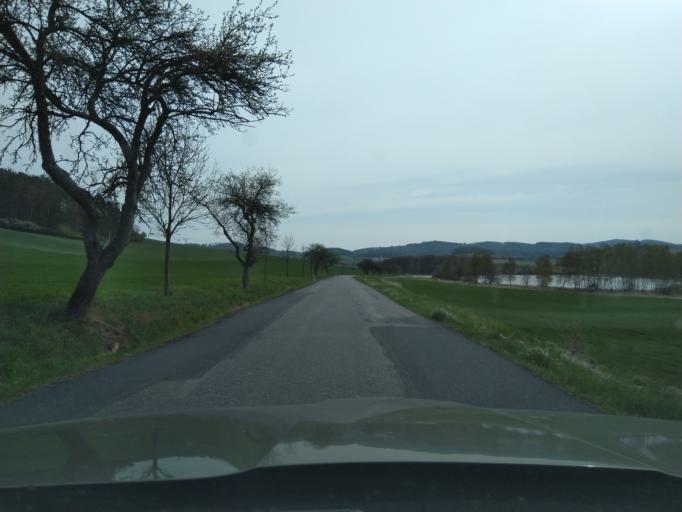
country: CZ
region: Plzensky
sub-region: Okres Klatovy
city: Susice
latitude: 49.2255
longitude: 13.5921
